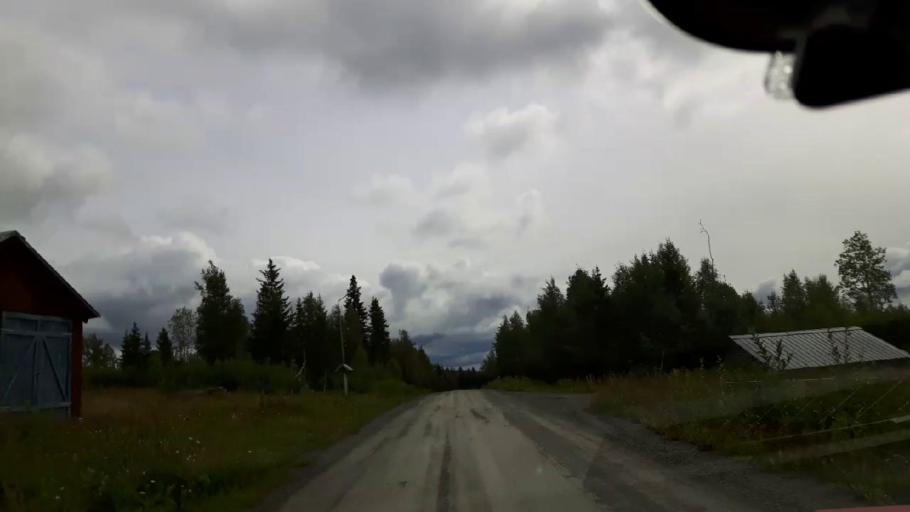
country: SE
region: Jaemtland
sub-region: Krokoms Kommun
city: Valla
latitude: 63.6703
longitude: 13.9563
